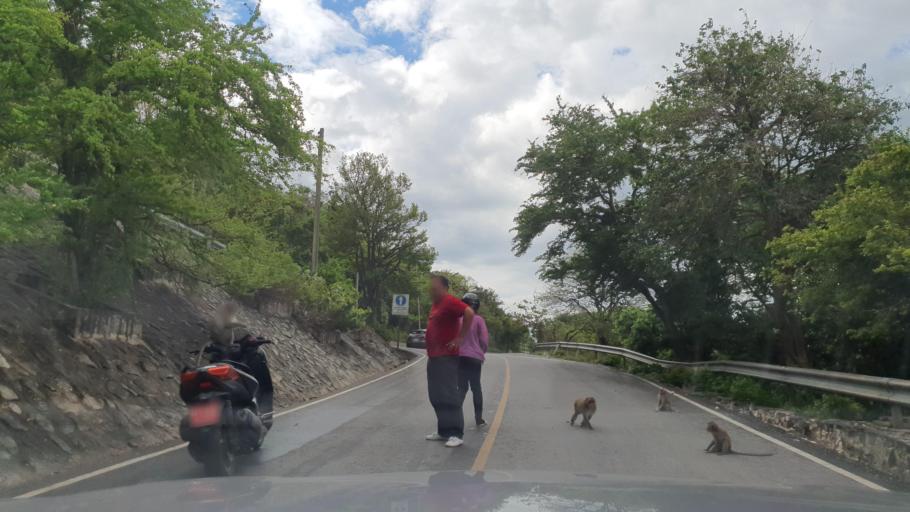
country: TH
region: Chon Buri
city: Chon Buri
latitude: 13.3122
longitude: 100.9039
